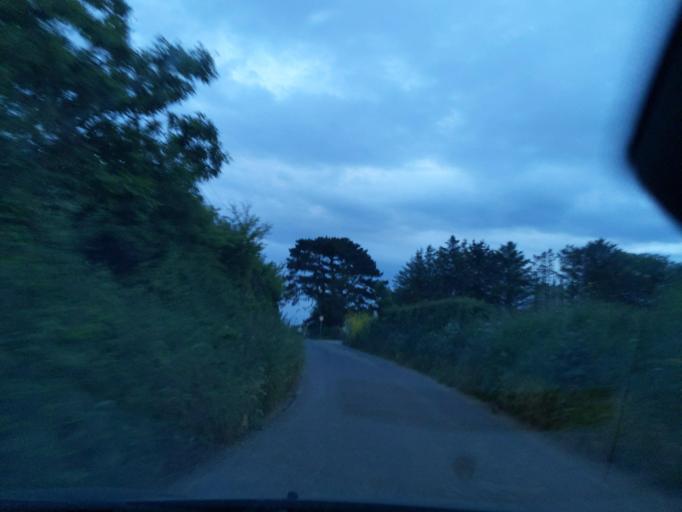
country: GB
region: England
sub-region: Cornwall
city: Wadebridge
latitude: 50.5746
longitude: -4.8297
